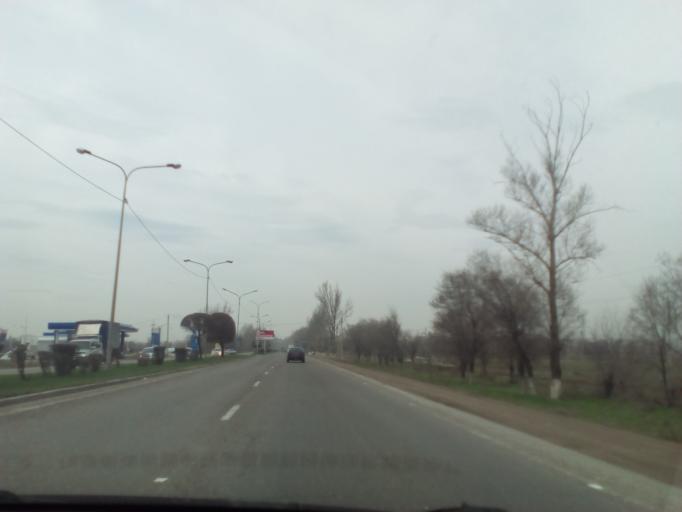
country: KZ
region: Almaty Oblysy
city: Burunday
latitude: 43.2215
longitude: 76.6242
